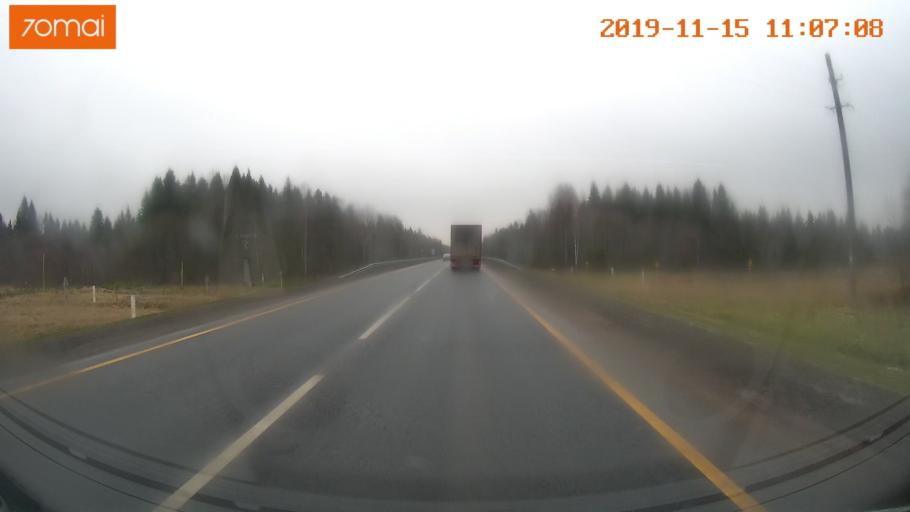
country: RU
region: Vologda
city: Chebsara
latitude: 59.1193
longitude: 39.0435
